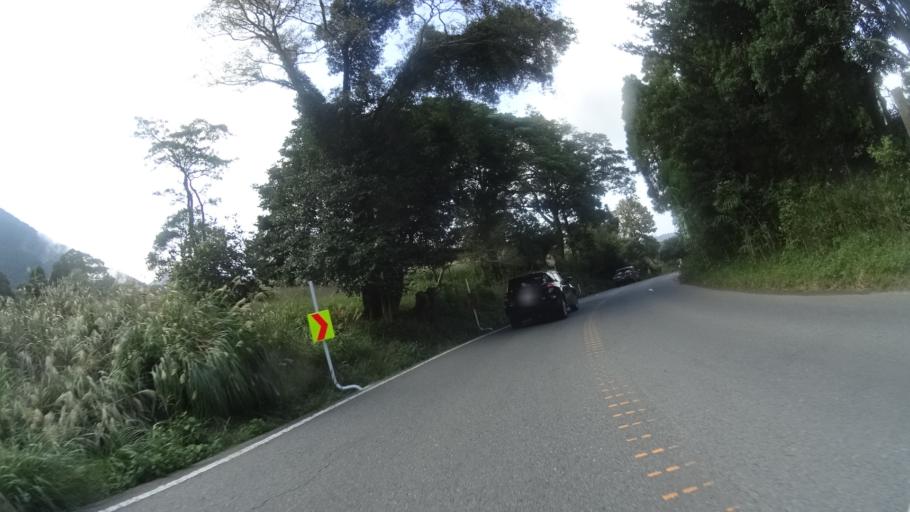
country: JP
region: Oita
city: Beppu
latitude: 33.2890
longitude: 131.4563
